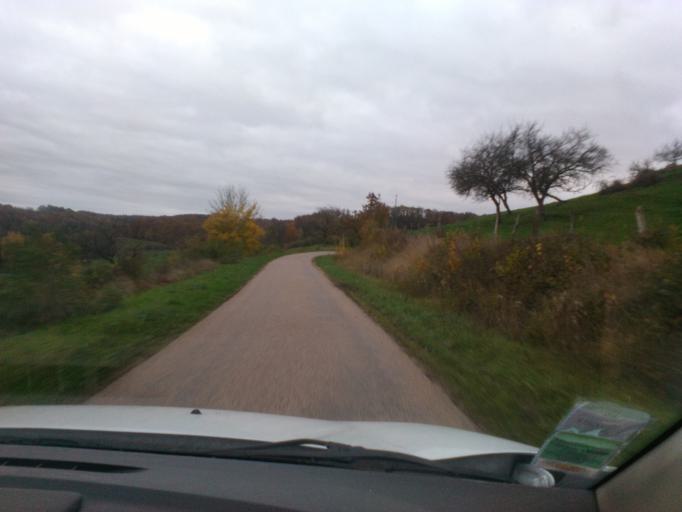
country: FR
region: Lorraine
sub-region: Departement des Vosges
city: Mirecourt
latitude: 48.3085
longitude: 6.2120
